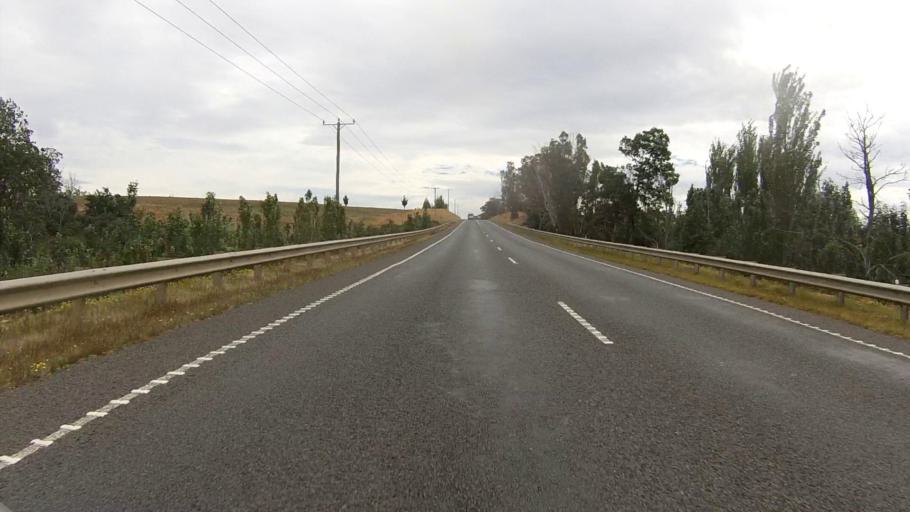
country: AU
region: Tasmania
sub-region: Northern Midlands
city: Evandale
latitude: -41.7011
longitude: 147.2923
